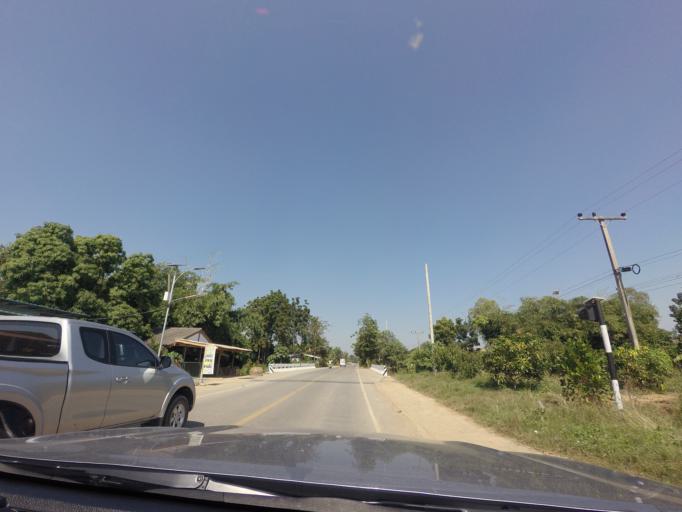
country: TH
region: Sukhothai
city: Si Samrong
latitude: 17.1319
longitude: 99.7778
